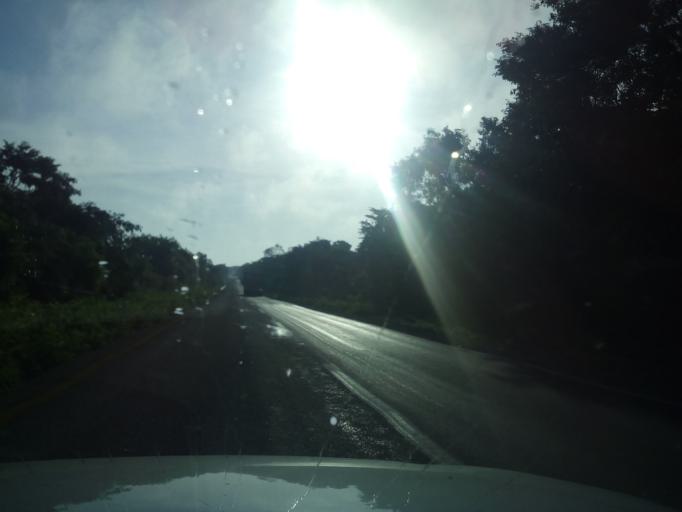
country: MX
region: Yucatan
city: Piste
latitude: 20.7461
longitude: -88.6969
